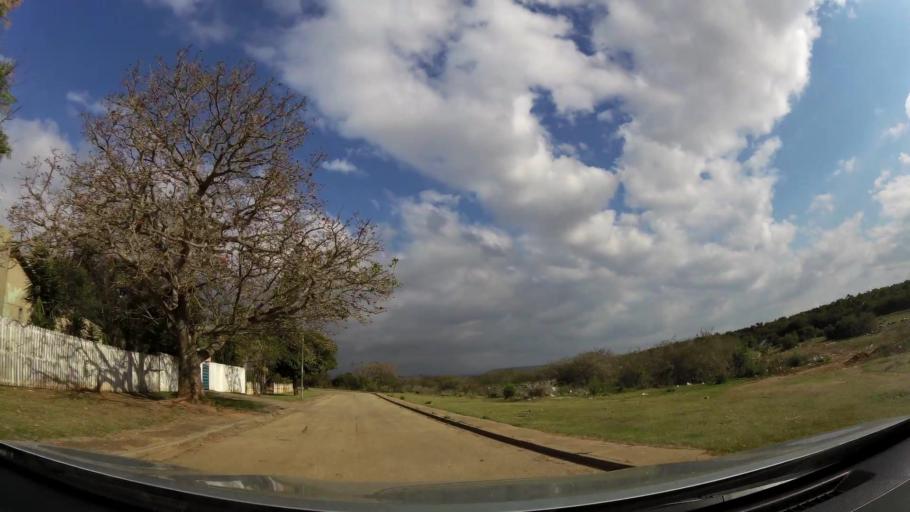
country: ZA
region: Eastern Cape
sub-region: Nelson Mandela Bay Metropolitan Municipality
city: Uitenhage
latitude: -33.7307
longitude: 25.4051
